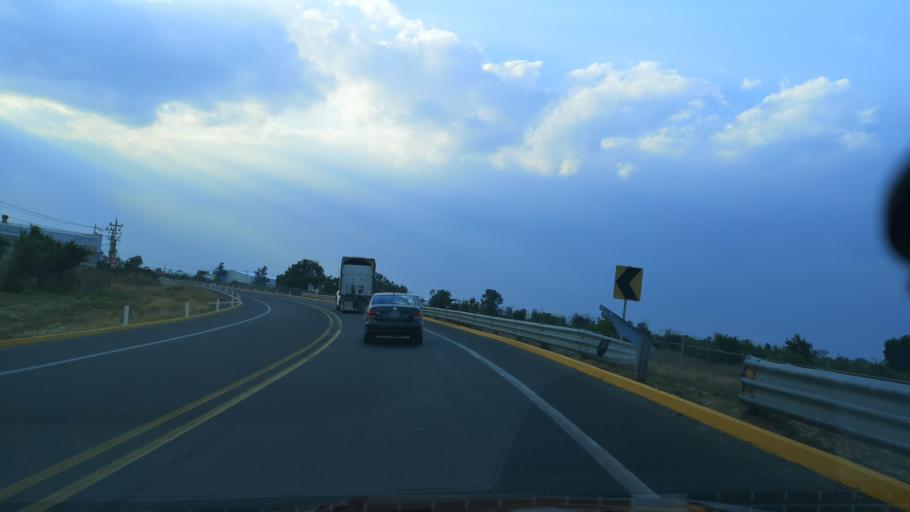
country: MX
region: Puebla
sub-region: Juan C. Bonilla
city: Santa Maria Zacatepec
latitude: 19.1516
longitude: -98.3745
